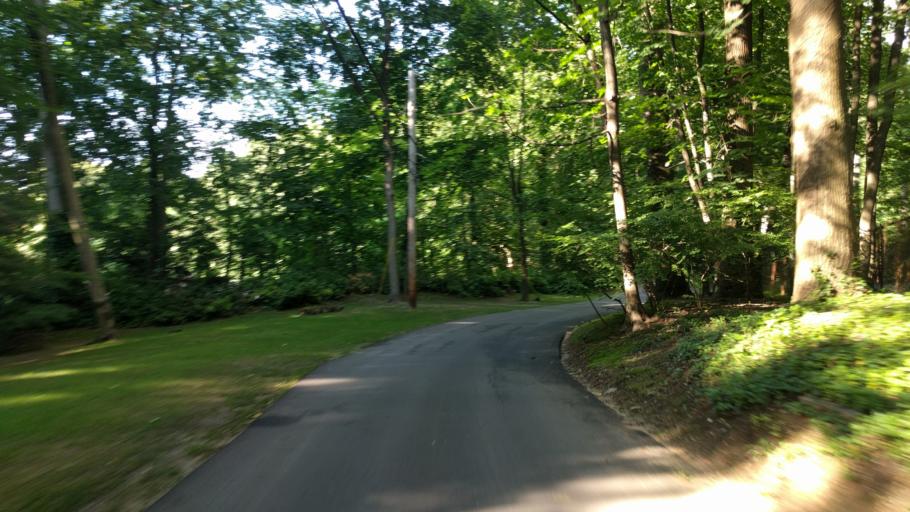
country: US
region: New York
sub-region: Nassau County
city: Oyster Bay Cove
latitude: 40.8692
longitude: -73.5116
